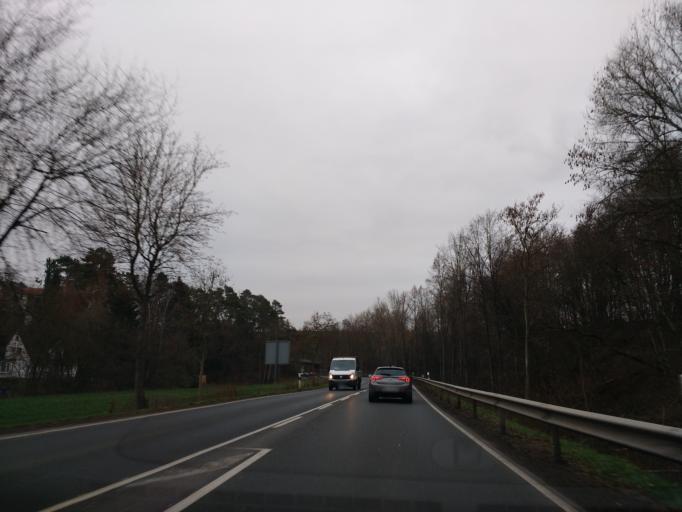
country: DE
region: Hesse
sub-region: Regierungsbezirk Kassel
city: Baunatal
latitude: 51.2140
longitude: 9.4354
